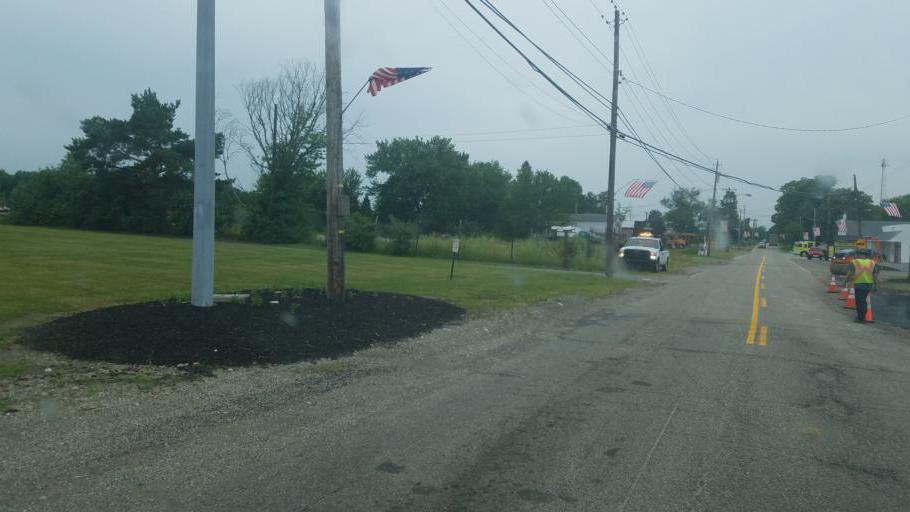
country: US
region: Ohio
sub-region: Portage County
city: Ravenna
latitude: 41.0997
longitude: -81.1484
